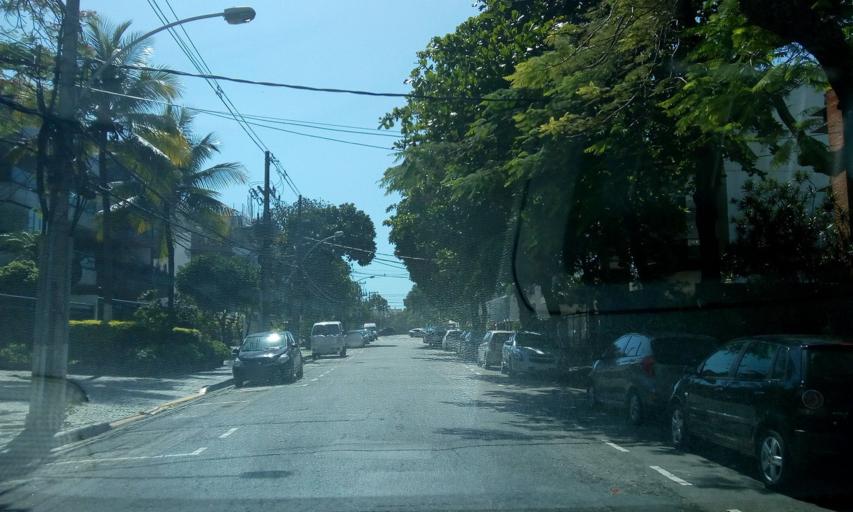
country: BR
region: Rio de Janeiro
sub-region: Rio De Janeiro
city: Rio de Janeiro
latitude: -23.0113
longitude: -43.3197
